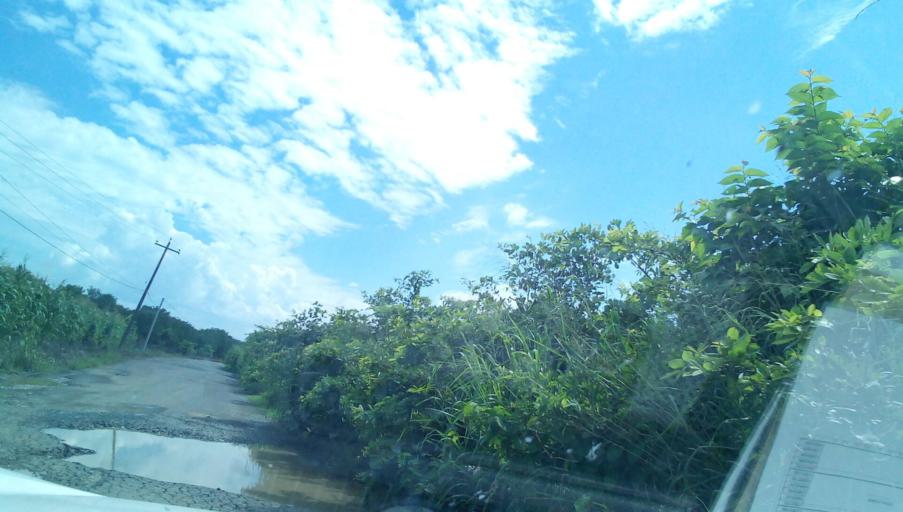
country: MX
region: Veracruz
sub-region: Alamo Temapache
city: Vegas de la Soledad y Soledad Dos
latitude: 20.9040
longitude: -97.9359
